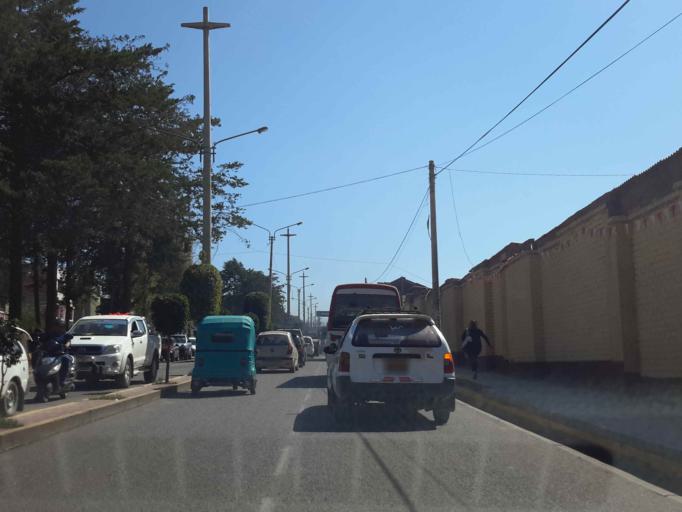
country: PE
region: Ayacucho
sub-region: Provincia de Huamanga
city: Ayacucho
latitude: -13.1531
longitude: -74.2234
